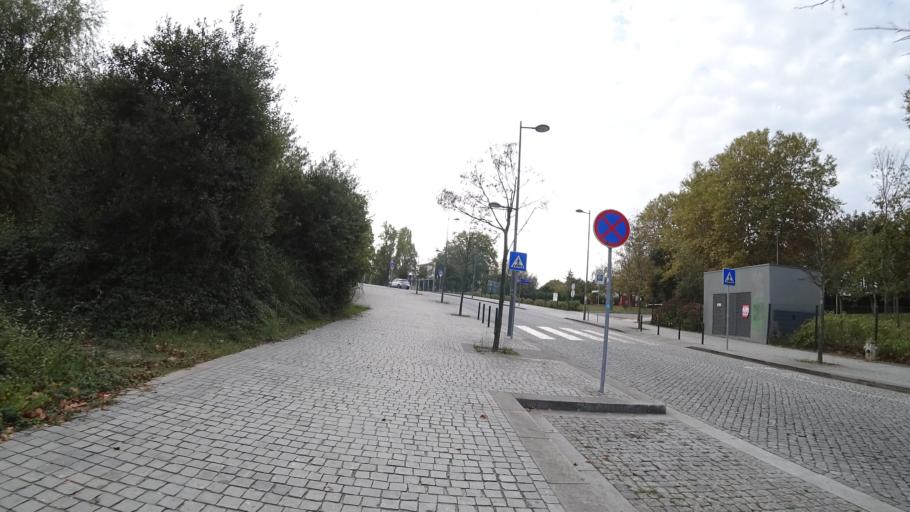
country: PT
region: Porto
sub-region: Matosinhos
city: Sao Mamede de Infesta
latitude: 41.1762
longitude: -8.6010
